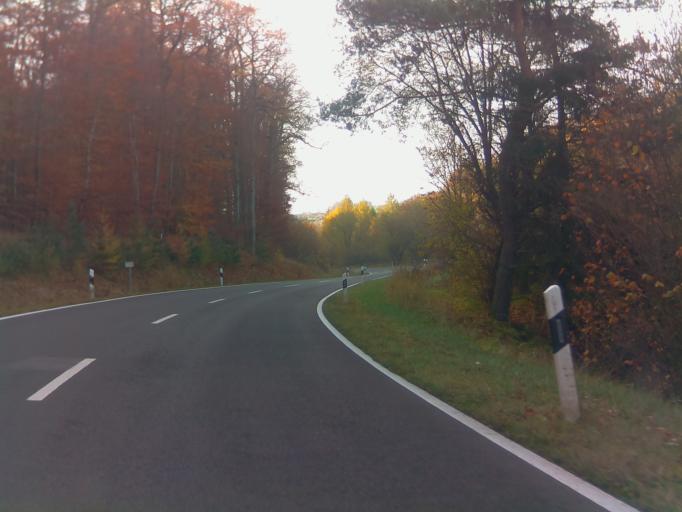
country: DE
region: Bavaria
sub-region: Regierungsbezirk Unterfranken
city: Burkardroth
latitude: 50.2503
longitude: 10.0171
